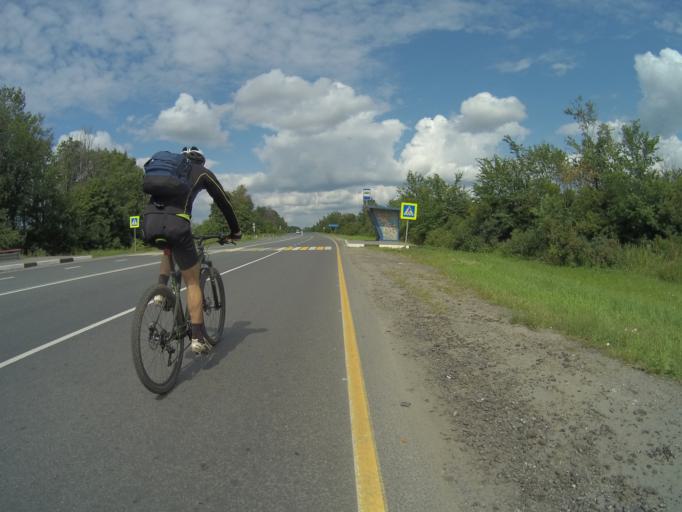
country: RU
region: Vladimir
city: Suzdal'
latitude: 56.3749
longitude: 40.4608
